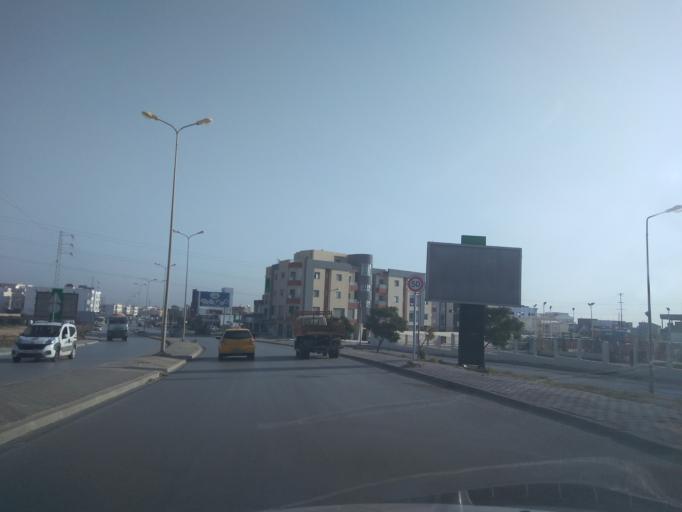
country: TN
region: Manouba
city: Manouba
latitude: 36.7858
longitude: 10.0815
